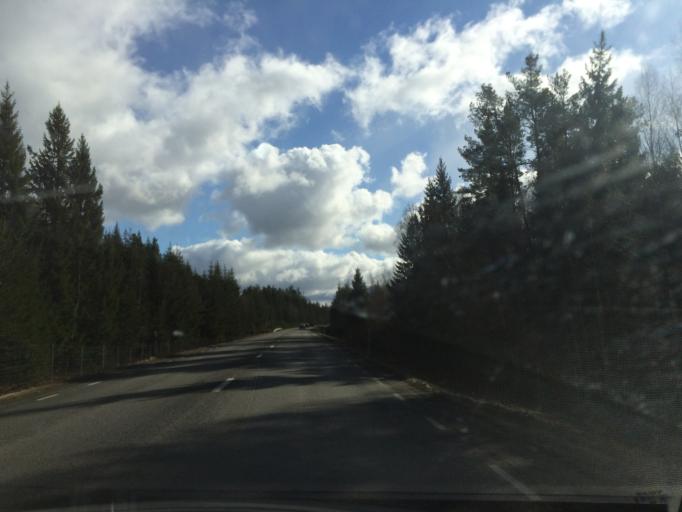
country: SE
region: Vaestra Goetaland
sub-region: Skara Kommun
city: Skara
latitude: 58.3585
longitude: 13.4252
